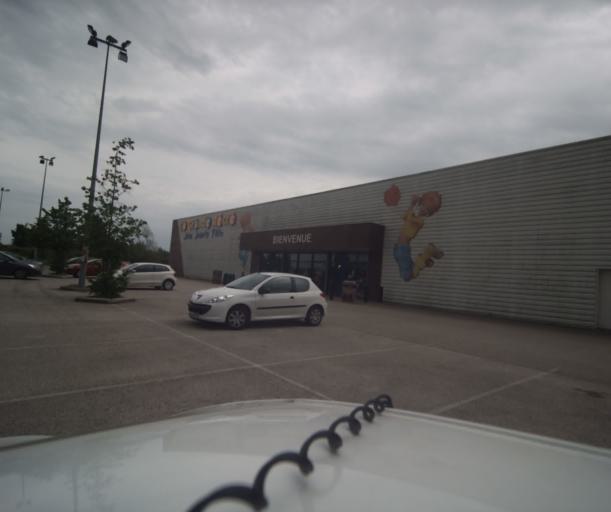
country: FR
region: Franche-Comte
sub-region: Departement du Doubs
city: Avanne-Aveney
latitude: 47.2188
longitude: 5.9549
